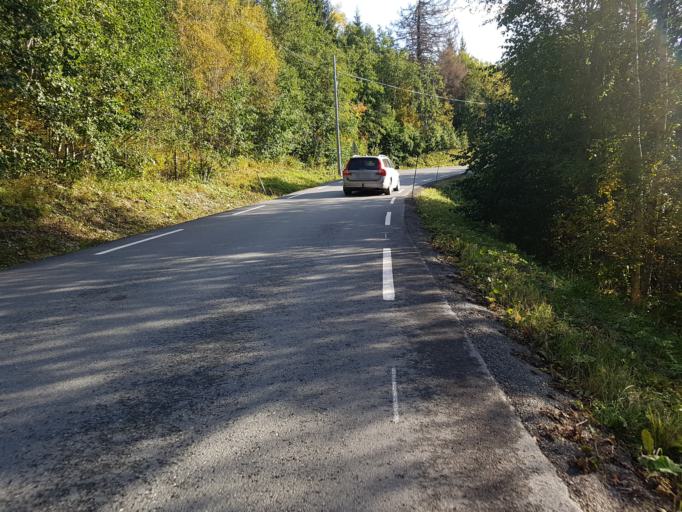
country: NO
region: Sor-Trondelag
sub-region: Malvik
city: Malvik
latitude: 63.3664
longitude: 10.6228
